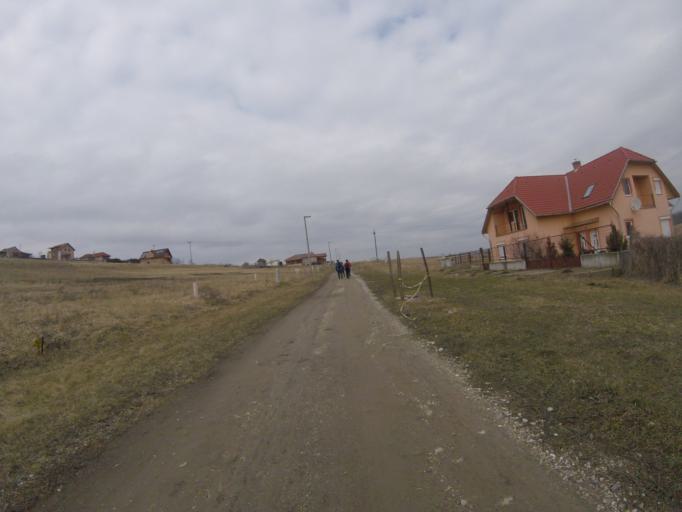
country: HU
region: Heves
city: Egerszalok
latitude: 47.8653
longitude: 20.3350
